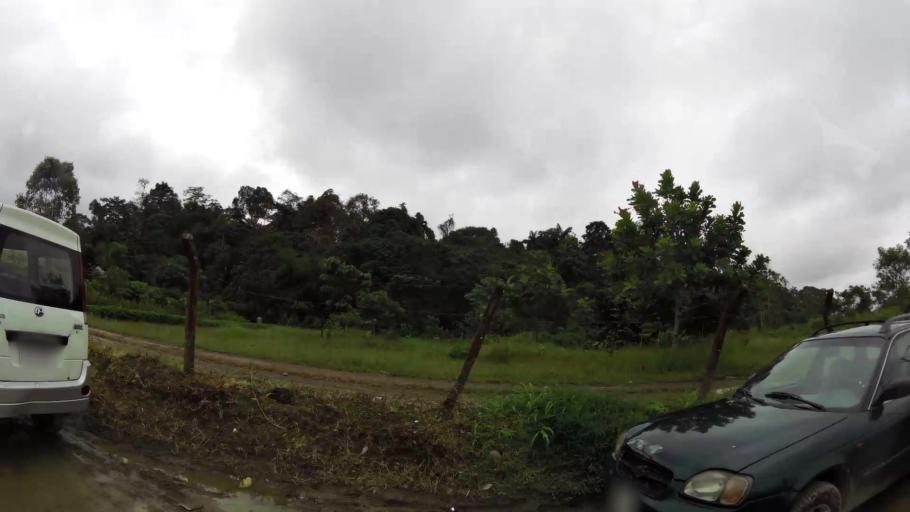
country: EC
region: Santo Domingo de los Tsachilas
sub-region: Canton Santo Domingo de los Colorados
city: Santo Domingo de los Colorados
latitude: -0.2514
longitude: -79.1457
